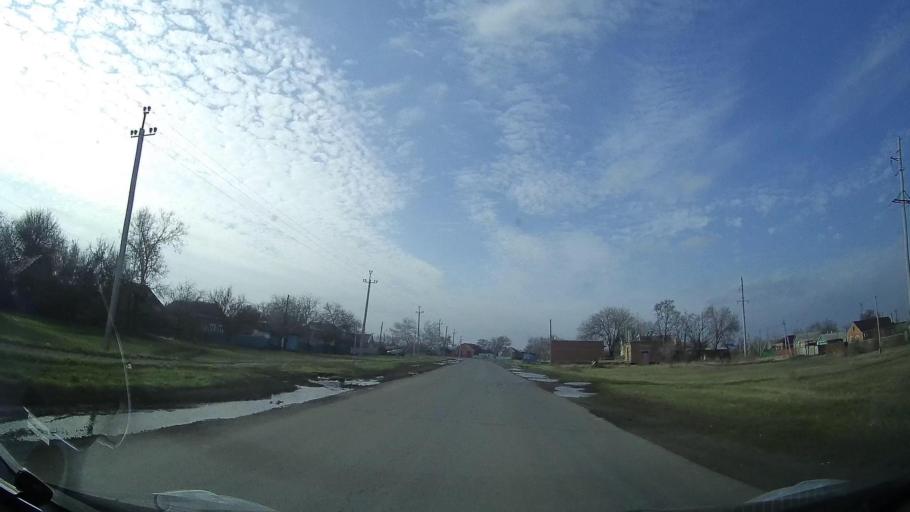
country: RU
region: Rostov
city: Mechetinskaya
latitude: 46.7872
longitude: 40.4743
